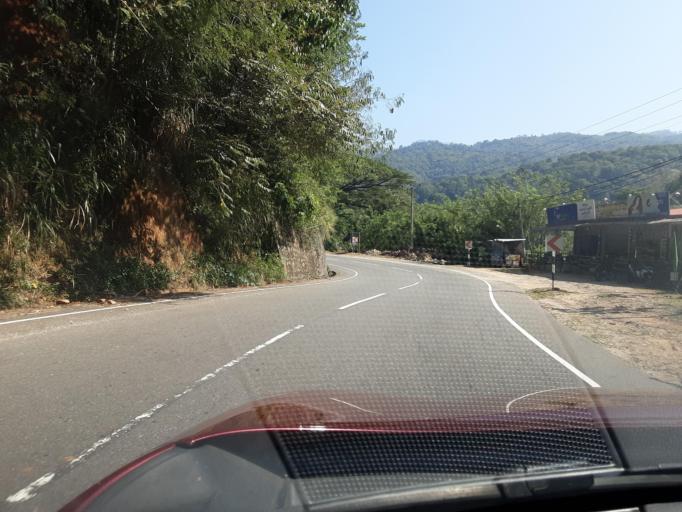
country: LK
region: Uva
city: Badulla
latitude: 7.0409
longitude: 81.0604
